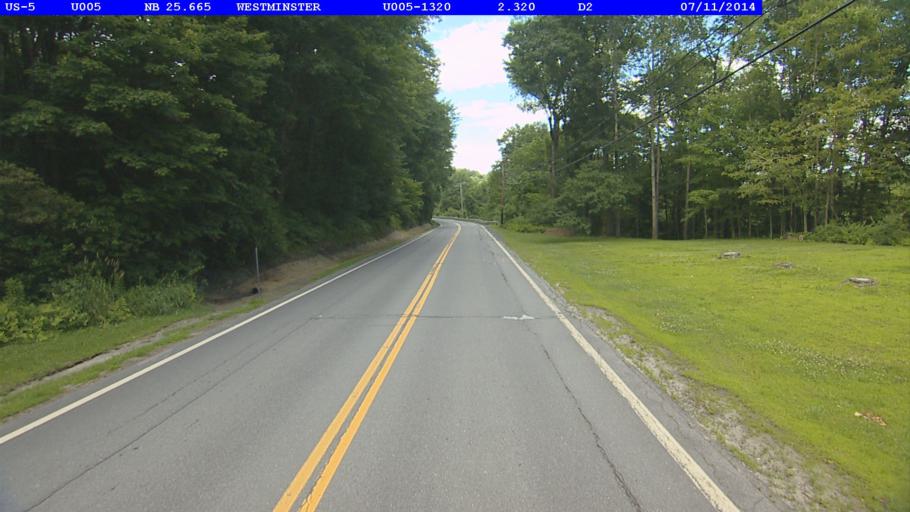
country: US
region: Vermont
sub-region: Windham County
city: Bellows Falls
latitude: 43.0524
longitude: -72.4692
